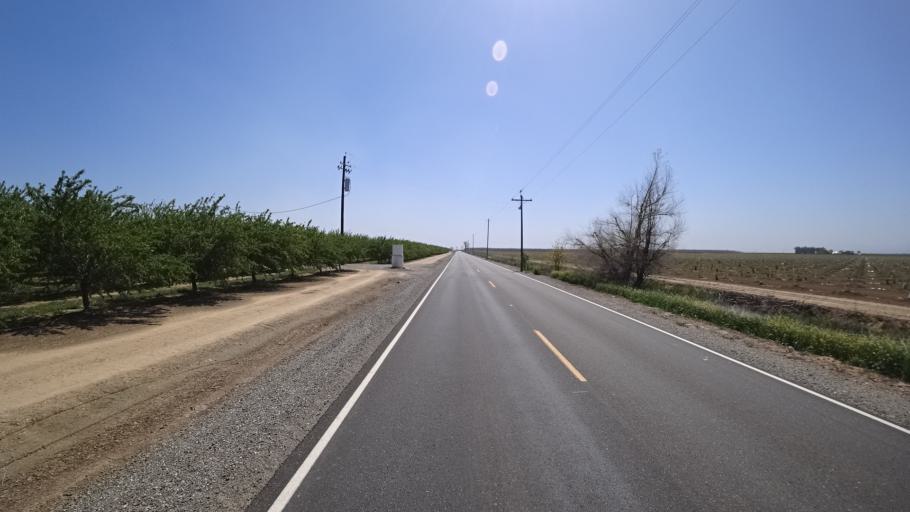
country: US
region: California
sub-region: Glenn County
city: Willows
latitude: 39.6186
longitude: -122.1376
